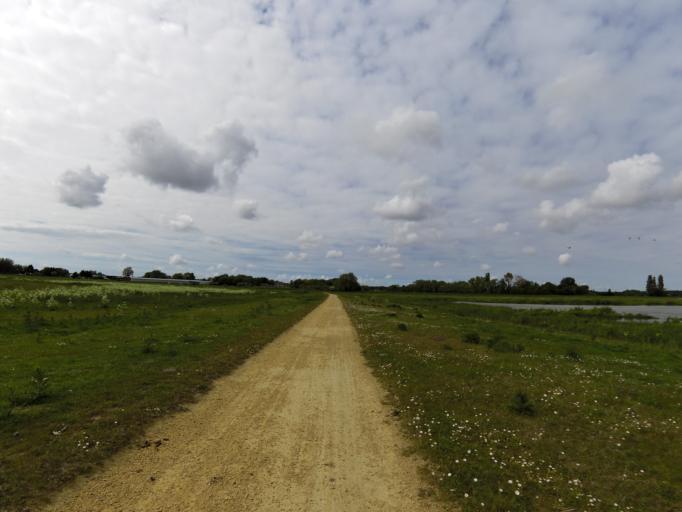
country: NL
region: South Holland
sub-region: Gemeente Hellevoetsluis
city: Nieuw-Helvoet
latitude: 51.8816
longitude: 4.0842
